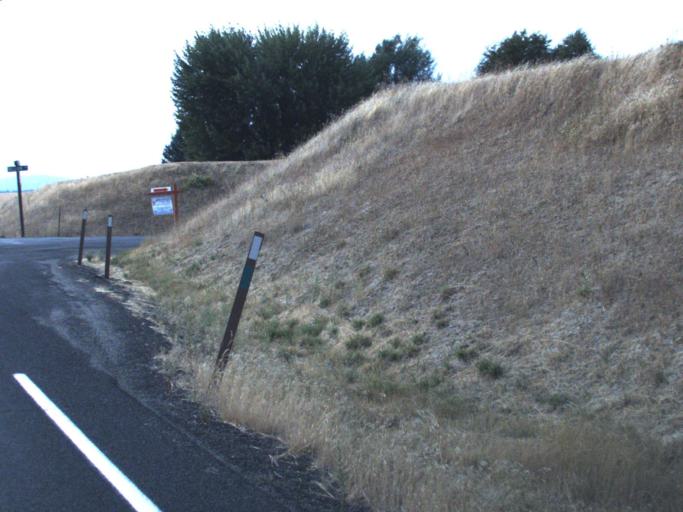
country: US
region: Washington
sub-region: Spokane County
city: Mead
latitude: 47.7875
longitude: -117.2786
